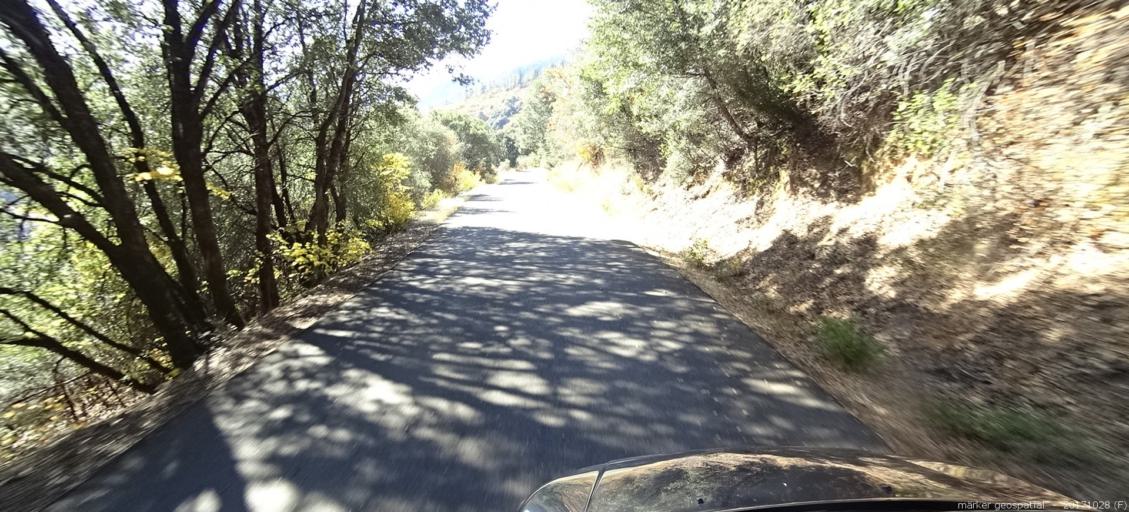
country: US
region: California
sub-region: Trinity County
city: Lewiston
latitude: 40.8047
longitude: -122.6106
